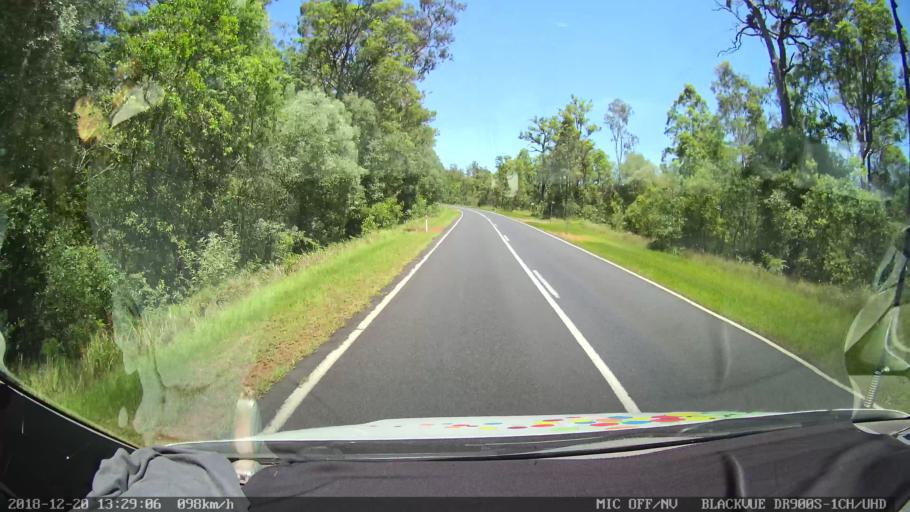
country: AU
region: New South Wales
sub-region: Clarence Valley
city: Gordon
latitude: -29.1843
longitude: 152.9889
